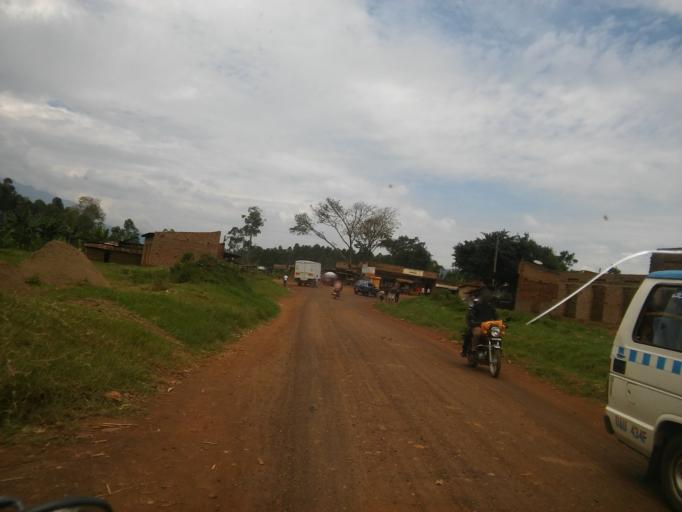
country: UG
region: Eastern Region
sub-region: Bududa District
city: Bududa
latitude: 0.9357
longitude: 34.2846
